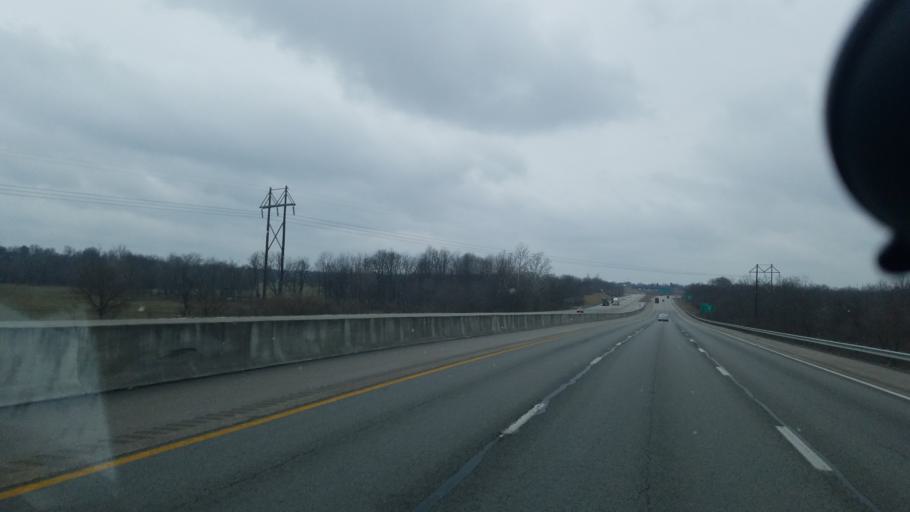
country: US
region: Kentucky
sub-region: Fayette County
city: Lexington-Fayette
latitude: 38.0592
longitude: -84.4113
